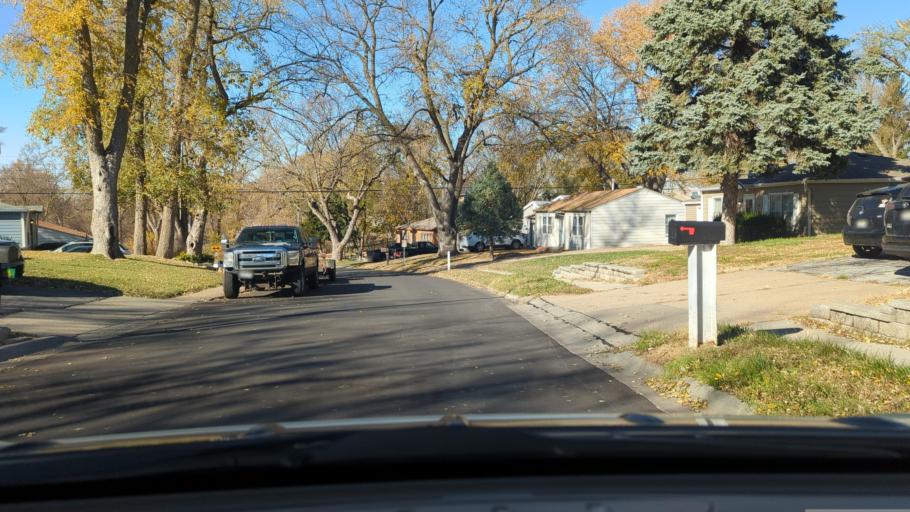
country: US
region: Nebraska
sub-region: Sarpy County
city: La Vista
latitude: 41.1853
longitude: -95.9758
